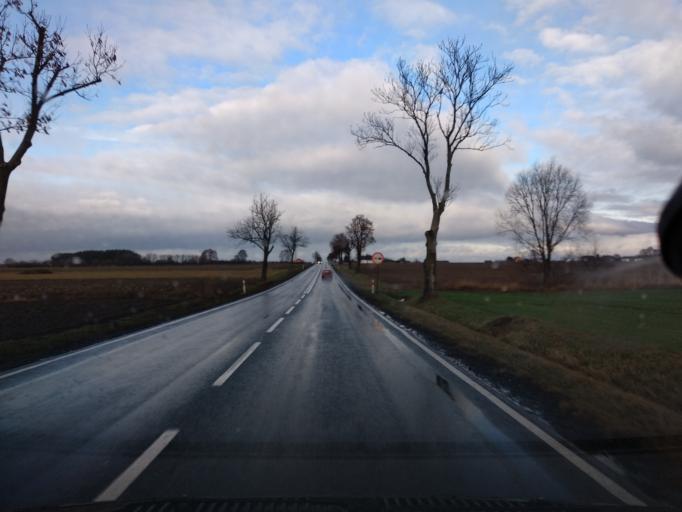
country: PL
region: Greater Poland Voivodeship
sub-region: Powiat koninski
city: Rychwal
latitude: 52.0478
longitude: 18.1626
